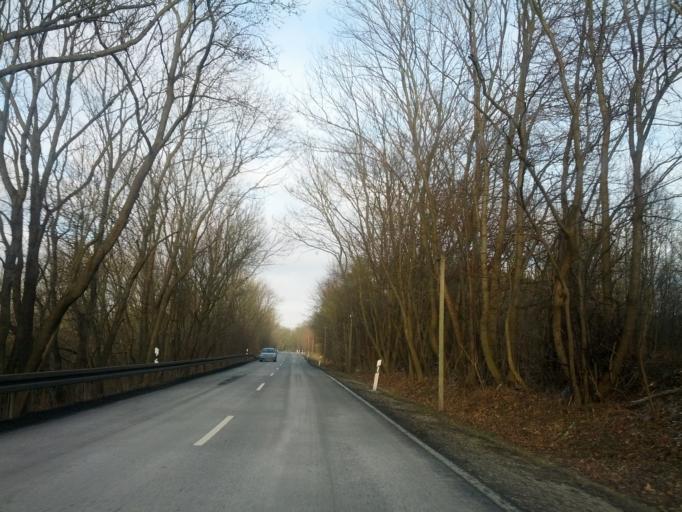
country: DE
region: Thuringia
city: Bad Langensalza
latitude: 51.0846
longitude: 10.6134
